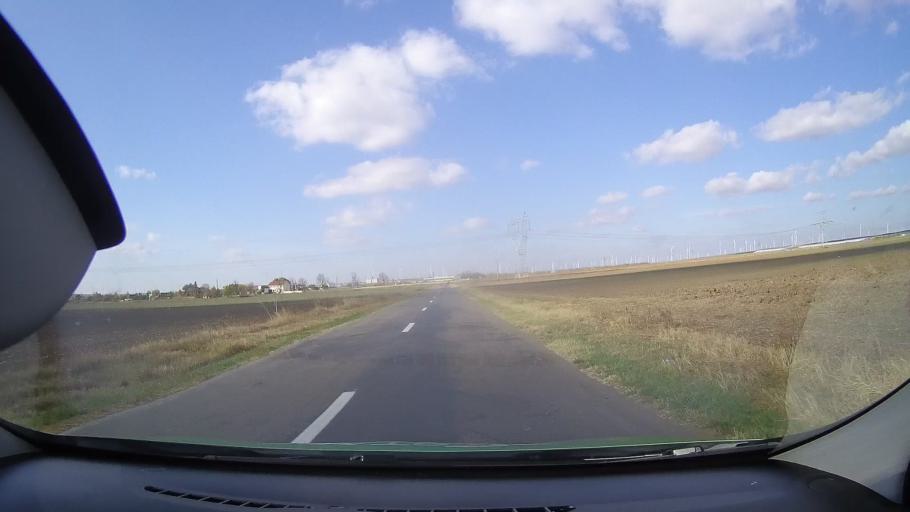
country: RO
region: Constanta
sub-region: Comuna Cogealac
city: Tariverde
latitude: 44.5573
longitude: 28.6146
